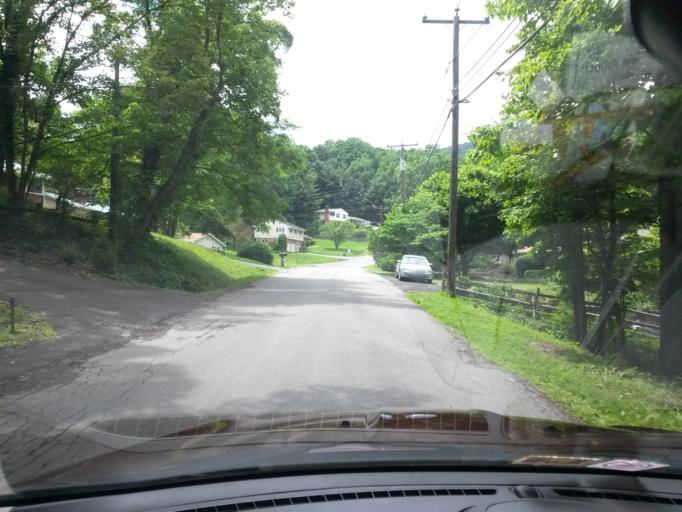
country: US
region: Virginia
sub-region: City of Covington
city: Fairlawn
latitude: 37.7825
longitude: -79.9199
